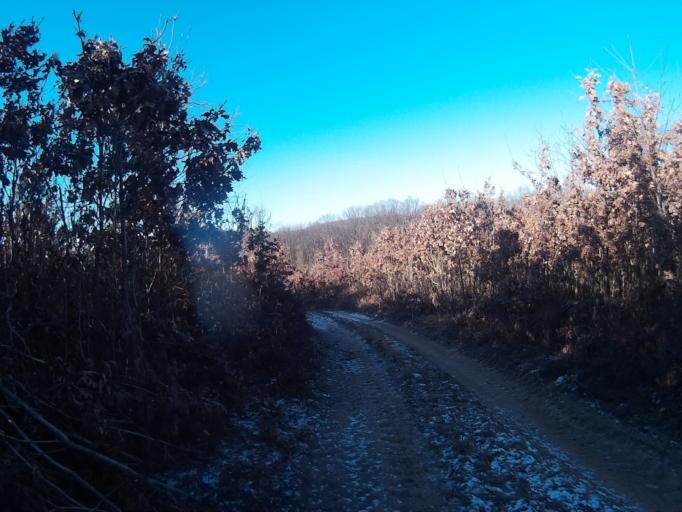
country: HU
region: Borsod-Abauj-Zemplen
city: Putnok
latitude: 48.4151
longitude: 20.4805
